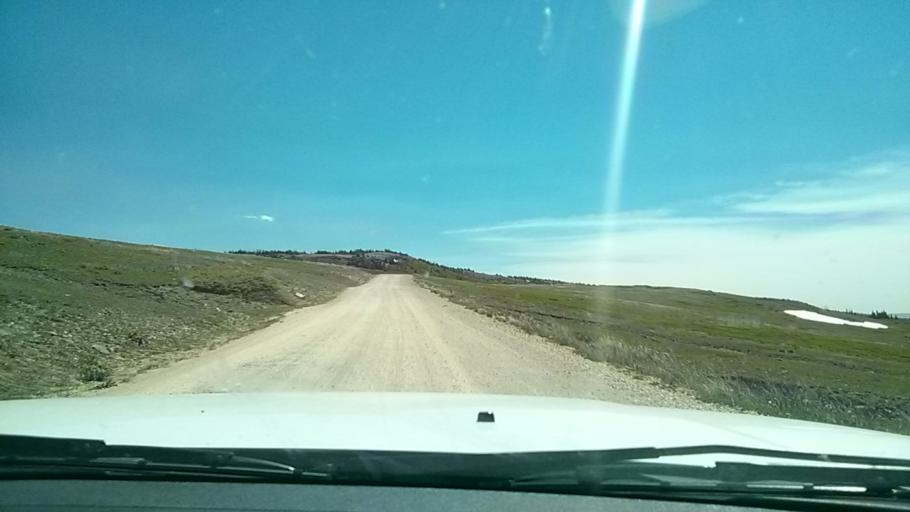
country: US
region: Utah
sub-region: Iron County
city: Parowan
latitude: 37.6728
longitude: -112.8305
